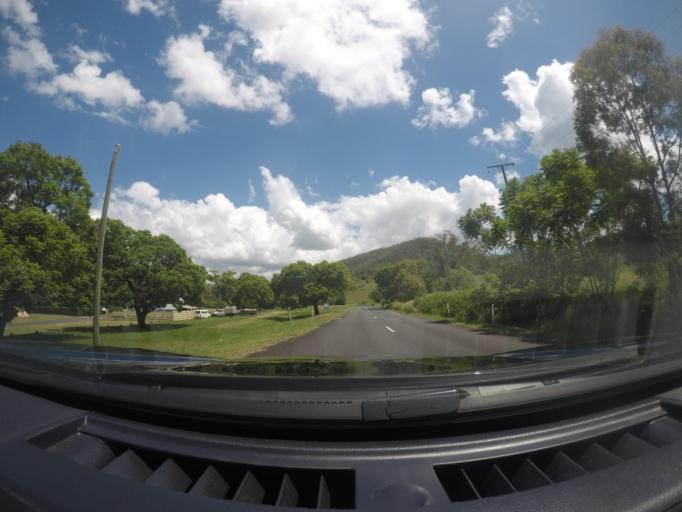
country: AU
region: Queensland
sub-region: Moreton Bay
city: Woodford
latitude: -27.1231
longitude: 152.5506
